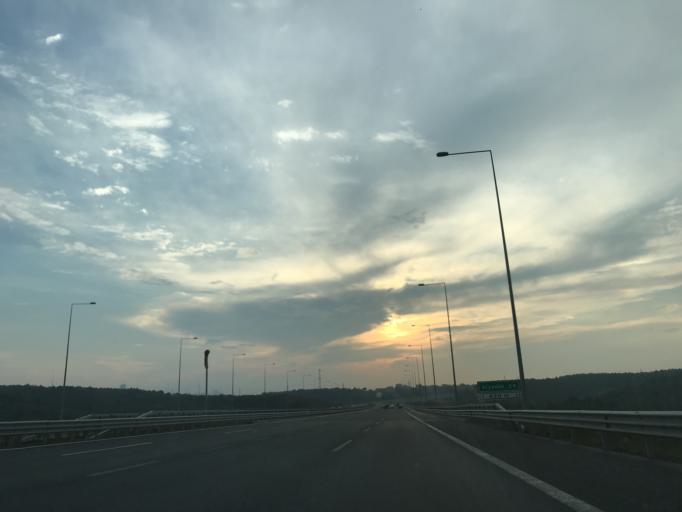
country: TR
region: Istanbul
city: Umraniye
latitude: 41.0496
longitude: 29.1391
